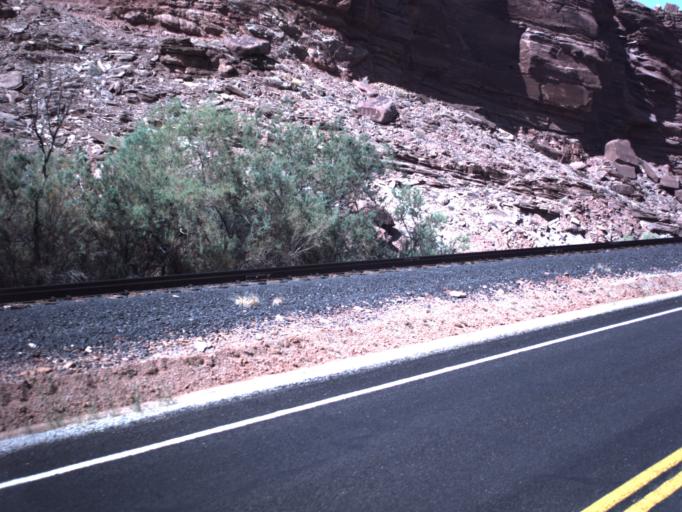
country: US
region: Utah
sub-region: Grand County
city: Moab
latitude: 38.5422
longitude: -109.6536
